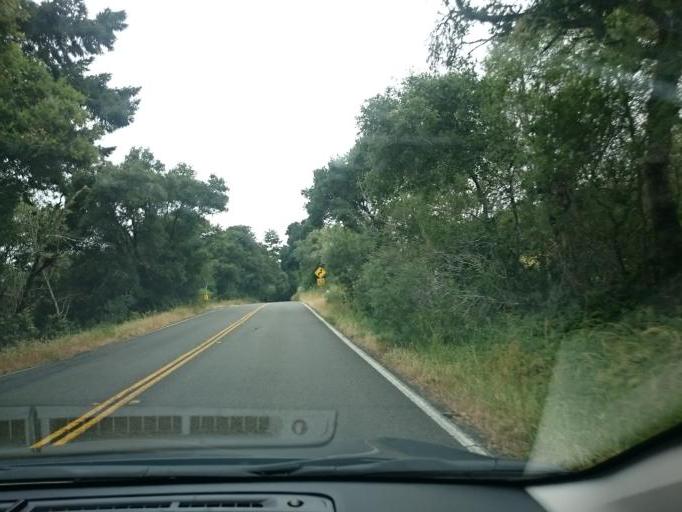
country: US
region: California
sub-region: Marin County
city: Lagunitas-Forest Knolls
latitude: 38.0224
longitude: -122.7738
